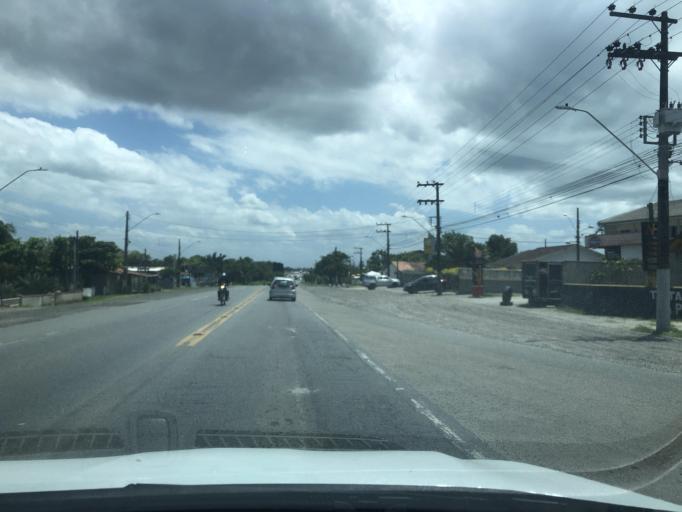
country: BR
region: Santa Catarina
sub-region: Joinville
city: Joinville
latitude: -26.3798
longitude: -48.7225
